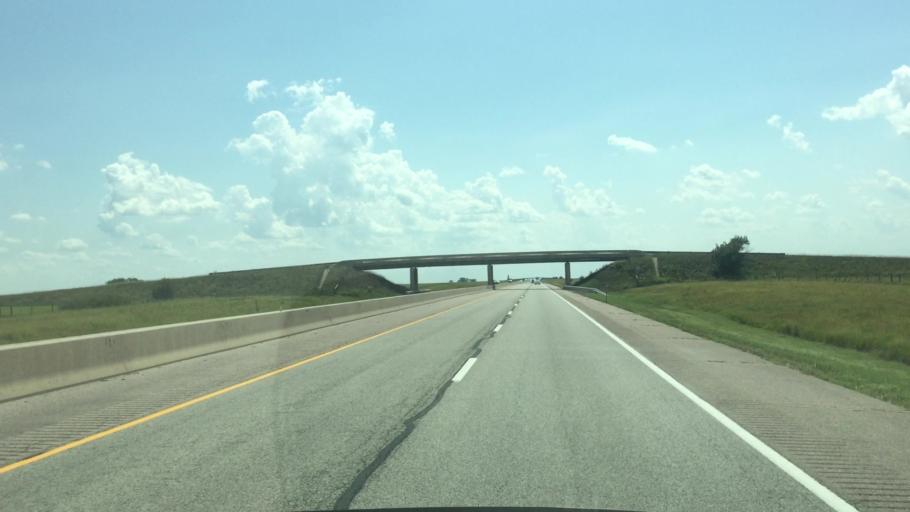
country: US
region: Kansas
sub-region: Butler County
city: El Dorado
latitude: 38.0149
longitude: -96.6748
